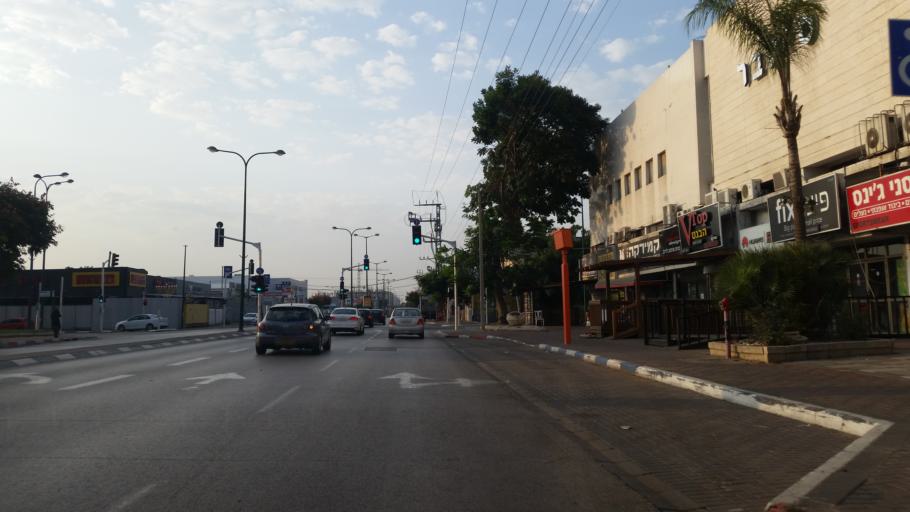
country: IL
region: Central District
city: Bet Yizhaq
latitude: 32.3208
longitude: 34.8743
